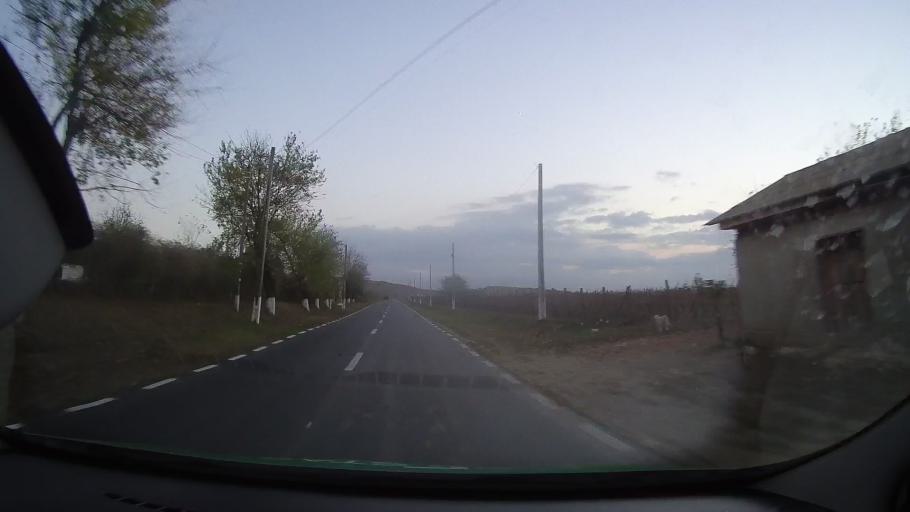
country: RO
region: Constanta
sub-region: Comuna Oltina
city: Oltina
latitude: 44.1570
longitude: 27.6674
